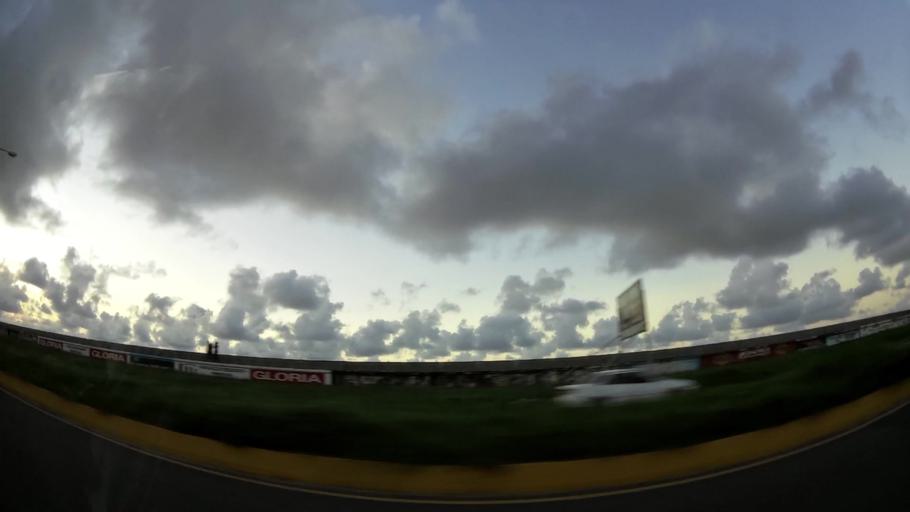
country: GY
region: Demerara-Mahaica
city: Georgetown
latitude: 6.8262
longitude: -58.1238
